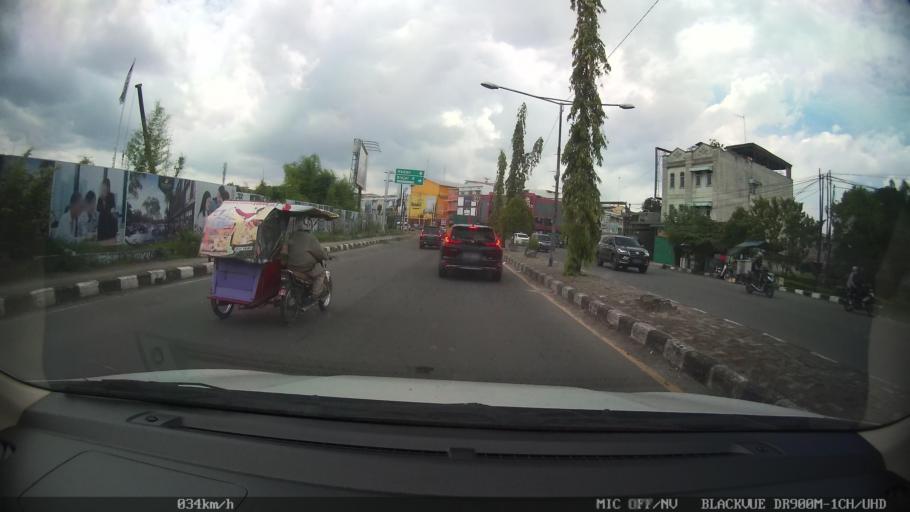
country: ID
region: North Sumatra
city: Medan
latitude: 3.6273
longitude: 98.6635
